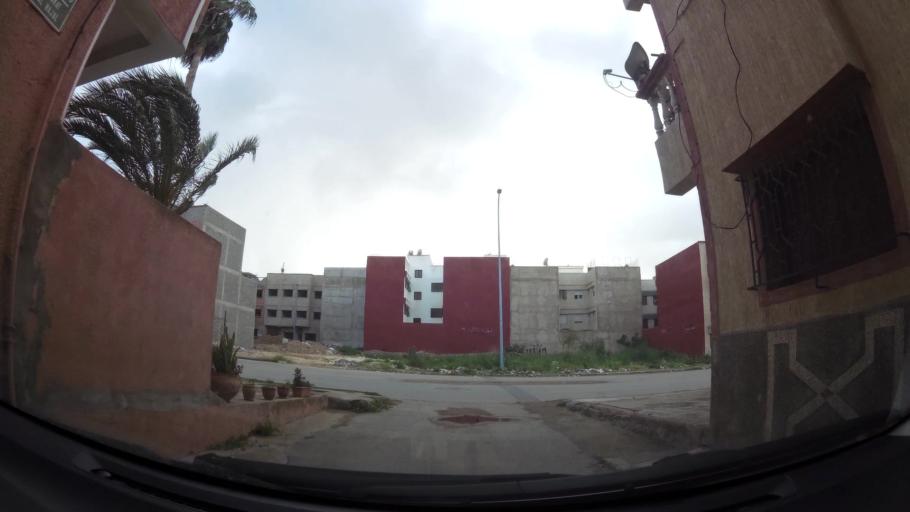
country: MA
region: Doukkala-Abda
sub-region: El-Jadida
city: El Jadida
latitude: 33.2459
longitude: -8.5284
